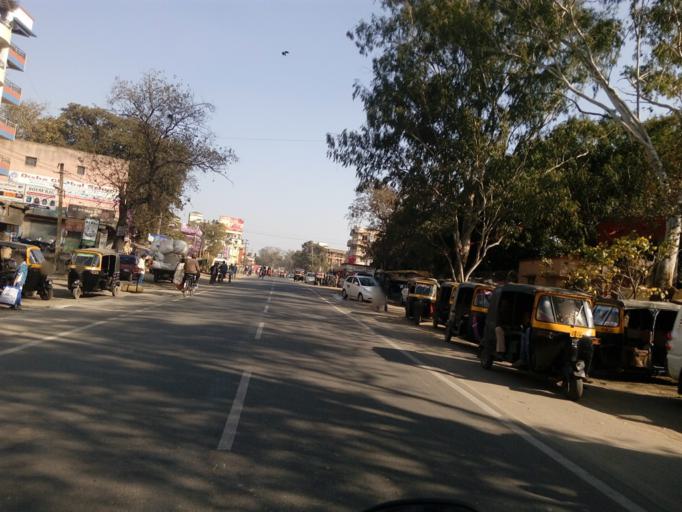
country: IN
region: Jharkhand
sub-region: Ranchi
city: Ranchi
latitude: 23.3611
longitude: 85.3543
